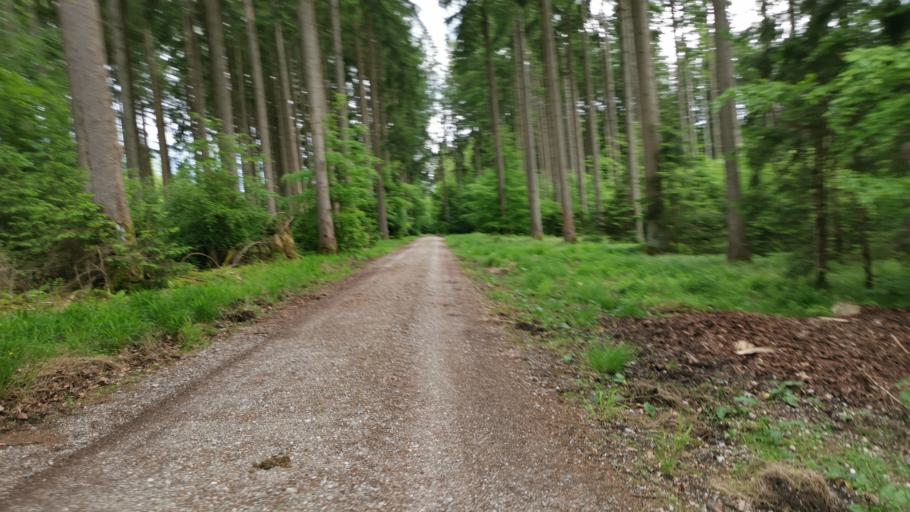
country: DE
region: Bavaria
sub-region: Upper Bavaria
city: Baierbrunn
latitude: 48.0276
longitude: 11.4578
